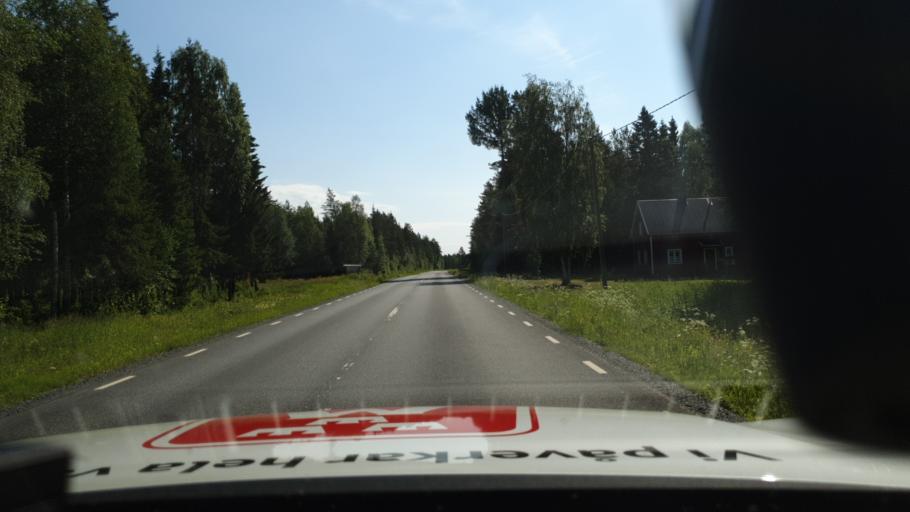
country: SE
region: Norrbotten
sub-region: Lulea Kommun
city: Gammelstad
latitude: 65.7878
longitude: 22.0911
